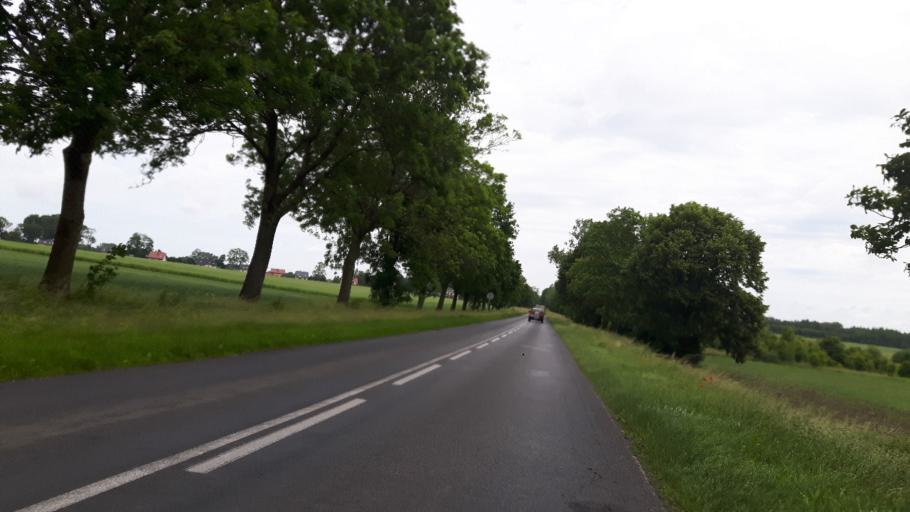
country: PL
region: West Pomeranian Voivodeship
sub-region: Powiat gryficki
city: Gryfice
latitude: 53.9368
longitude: 15.2165
